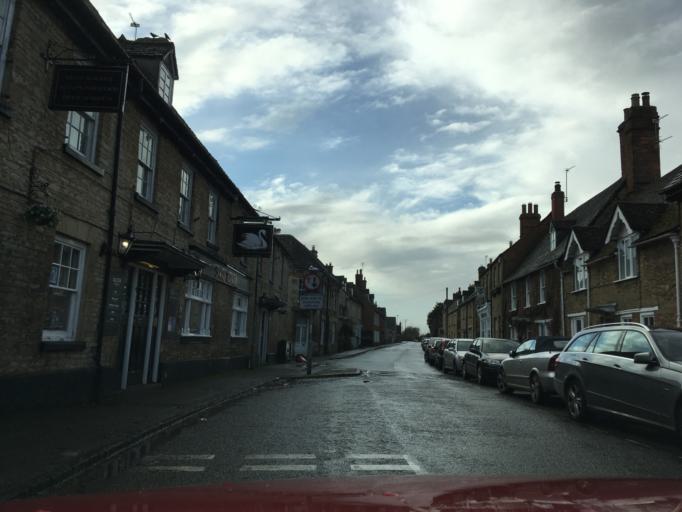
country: GB
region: England
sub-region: Oxfordshire
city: Eynsham
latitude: 51.7806
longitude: -1.3766
